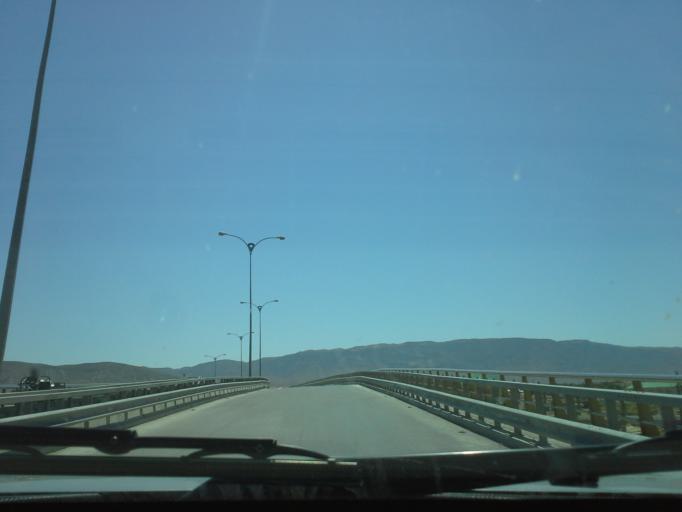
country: TM
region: Balkan
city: Serdar
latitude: 38.9799
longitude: 56.2784
